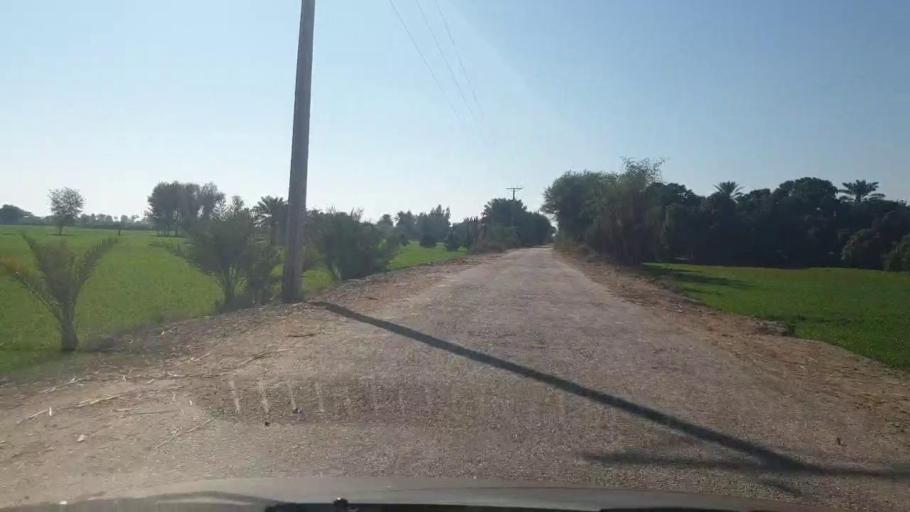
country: PK
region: Sindh
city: Bozdar
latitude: 27.2624
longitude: 68.6533
